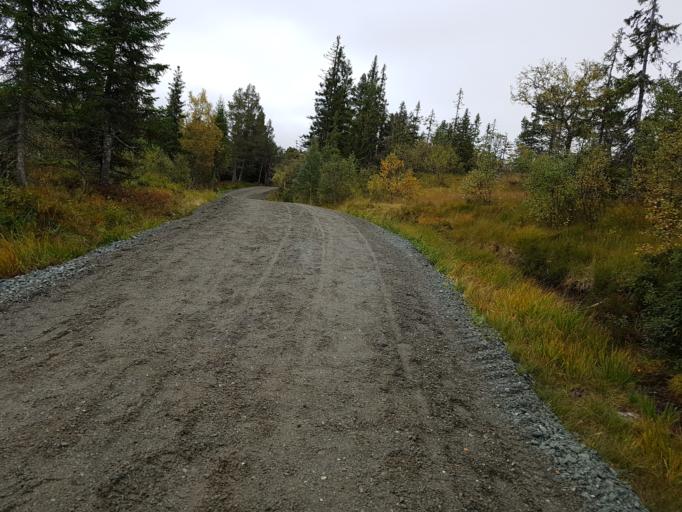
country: NO
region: Sor-Trondelag
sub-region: Melhus
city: Melhus
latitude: 63.4164
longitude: 10.2288
